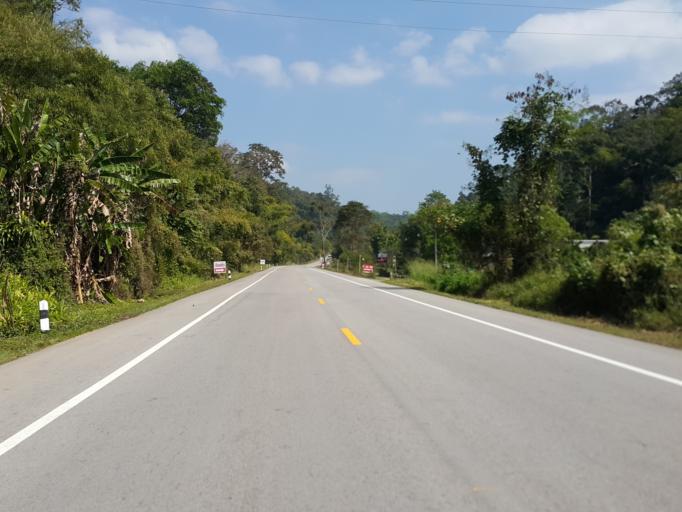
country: TH
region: Chiang Mai
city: Mae On
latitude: 19.0444
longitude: 99.3410
